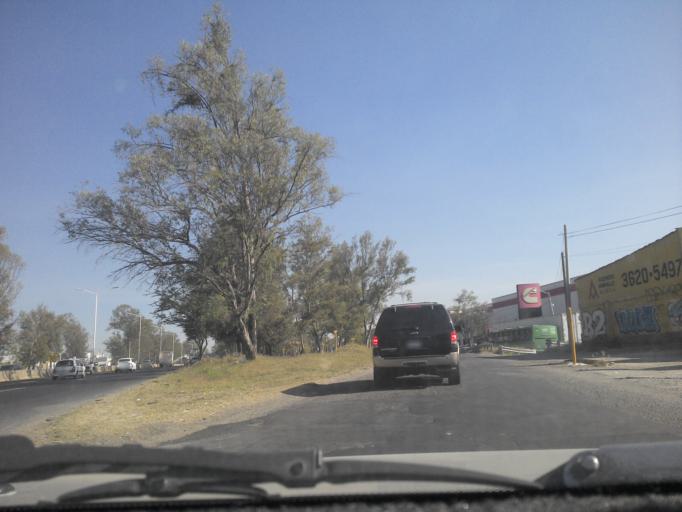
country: MX
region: Jalisco
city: Guadalajara
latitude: 20.6530
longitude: -103.4452
